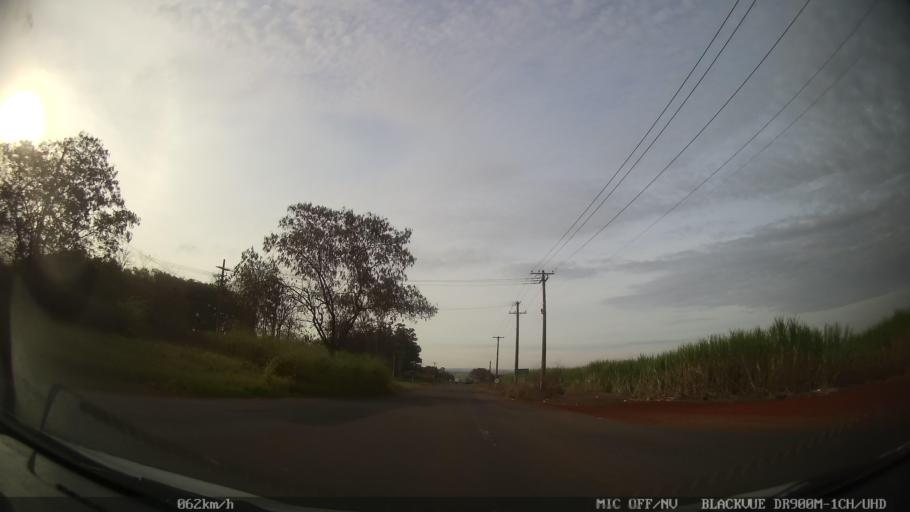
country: BR
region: Sao Paulo
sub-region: Piracicaba
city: Piracicaba
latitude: -22.7218
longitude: -47.5839
